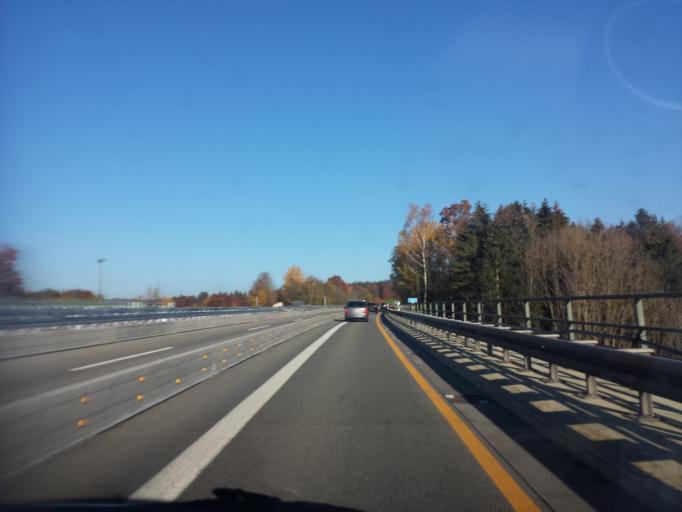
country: DE
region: Bavaria
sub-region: Upper Bavaria
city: Ohlstadt
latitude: 47.6615
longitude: 11.2437
